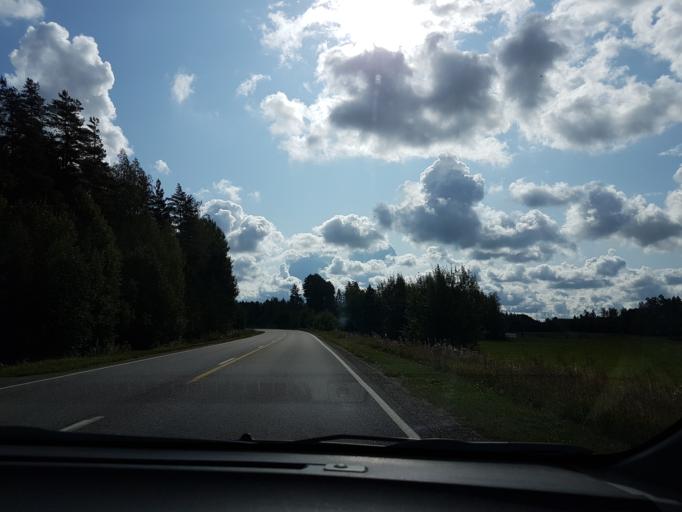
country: FI
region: Uusimaa
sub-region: Helsinki
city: Nickby
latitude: 60.4680
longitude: 25.2771
